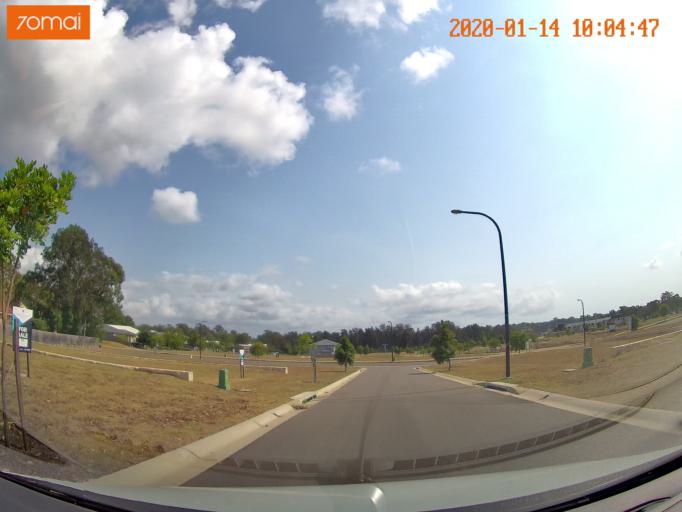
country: AU
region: New South Wales
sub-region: Wyong Shire
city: Kingfisher Shores
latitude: -33.1263
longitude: 151.5375
